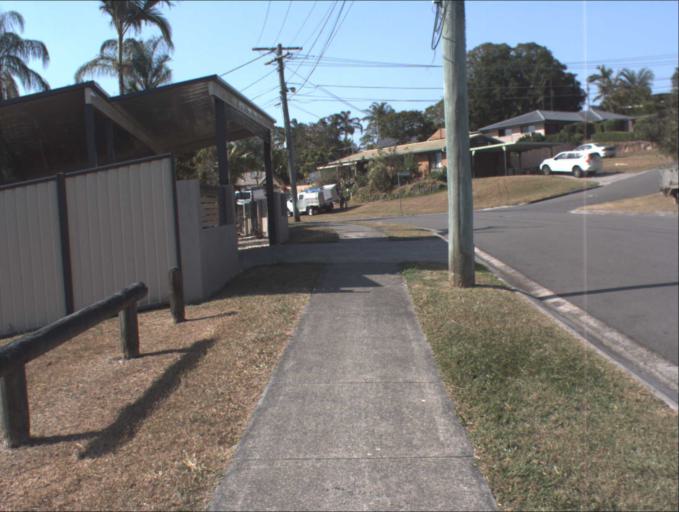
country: AU
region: Queensland
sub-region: Logan
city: Beenleigh
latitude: -27.6959
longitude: 153.1761
